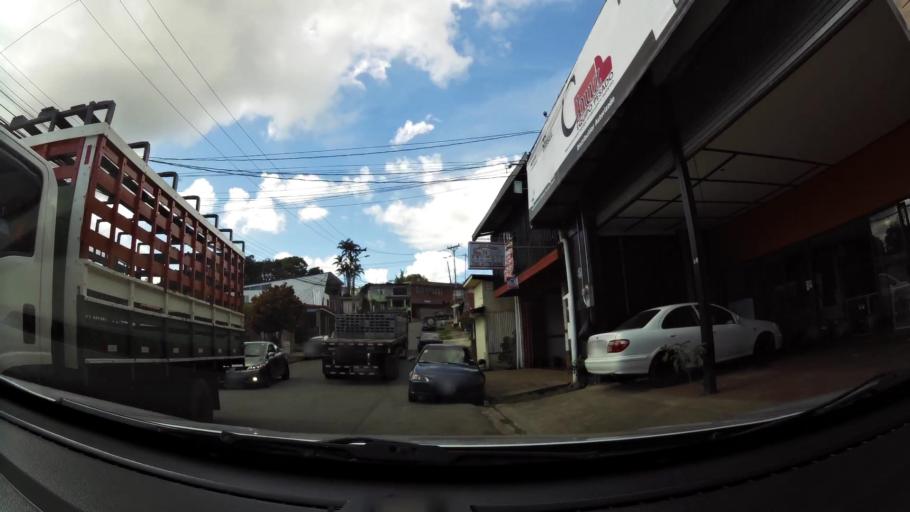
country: CR
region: San Jose
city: San Isidro
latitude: 9.3778
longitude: -83.7055
